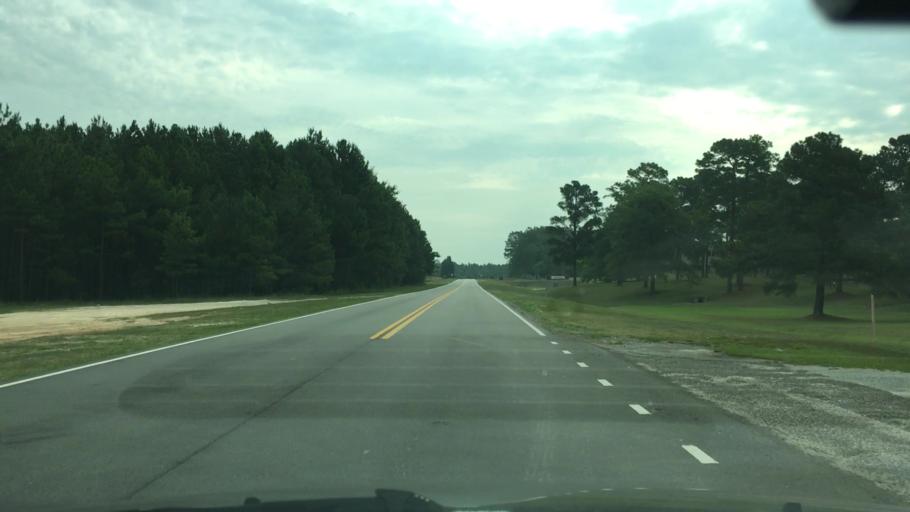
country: US
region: South Carolina
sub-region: Aiken County
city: Aiken
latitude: 33.6550
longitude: -81.6875
